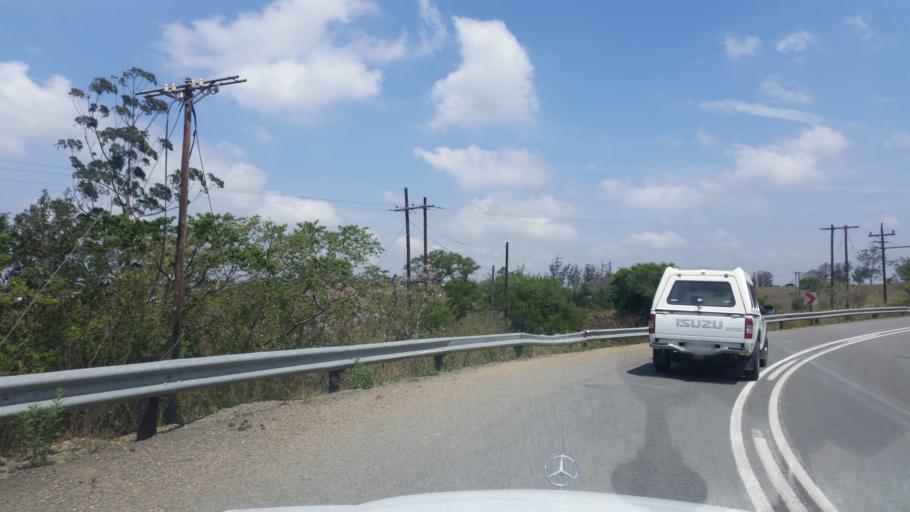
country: ZA
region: KwaZulu-Natal
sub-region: uMgungundlovu District Municipality
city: Camperdown
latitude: -29.6985
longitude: 30.4940
